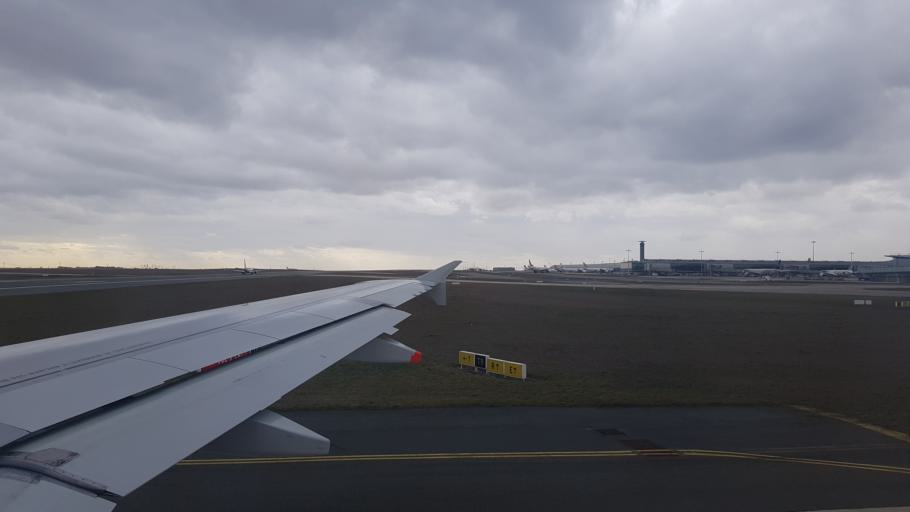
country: FR
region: Ile-de-France
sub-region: Departement de Seine-et-Marne
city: Mitry-Mory
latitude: 48.9990
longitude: 2.5966
